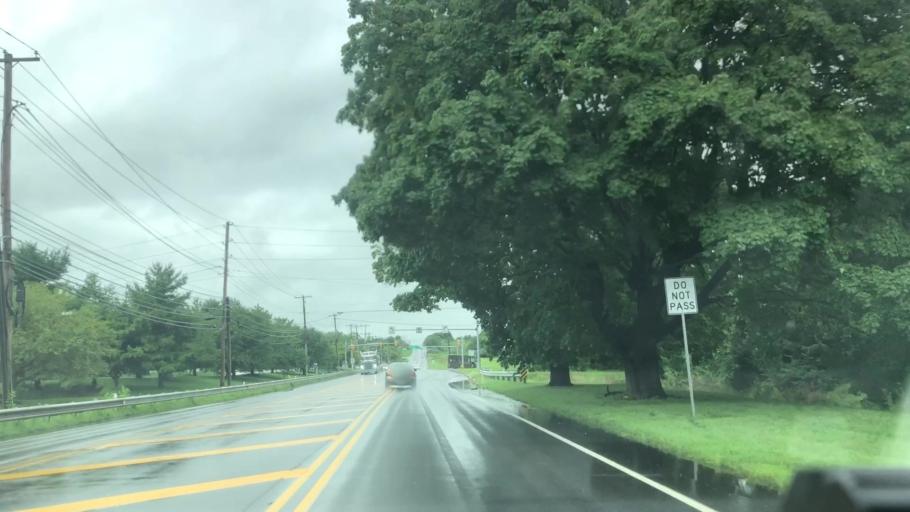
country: US
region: Pennsylvania
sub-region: Lehigh County
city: Trexlertown
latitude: 40.5875
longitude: -75.6120
